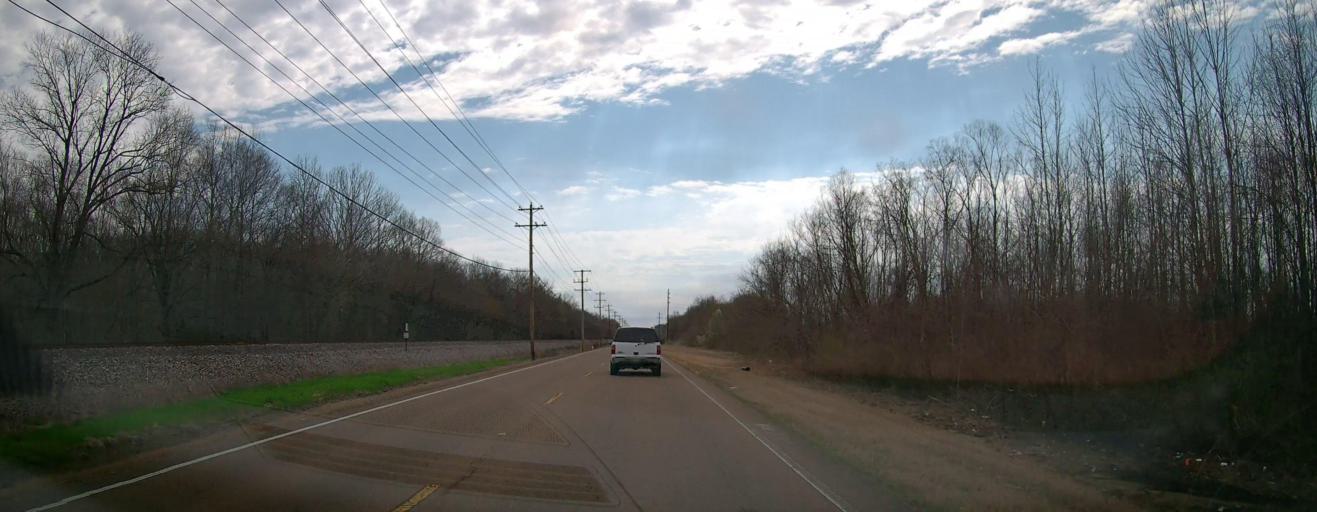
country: US
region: Mississippi
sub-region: Marshall County
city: Byhalia
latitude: 34.9115
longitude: -89.7594
